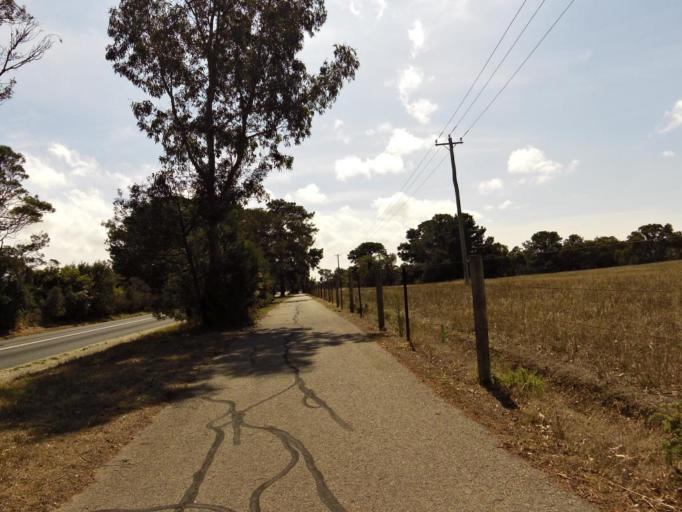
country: AU
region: Victoria
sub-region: Mornington Peninsula
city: Crib Point
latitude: -38.3639
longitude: 145.1708
